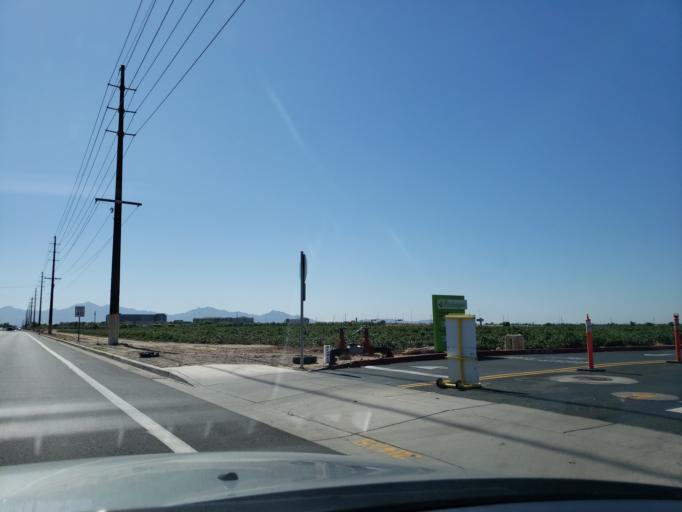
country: US
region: Arizona
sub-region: Maricopa County
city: Tolleson
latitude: 33.4897
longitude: -112.2553
